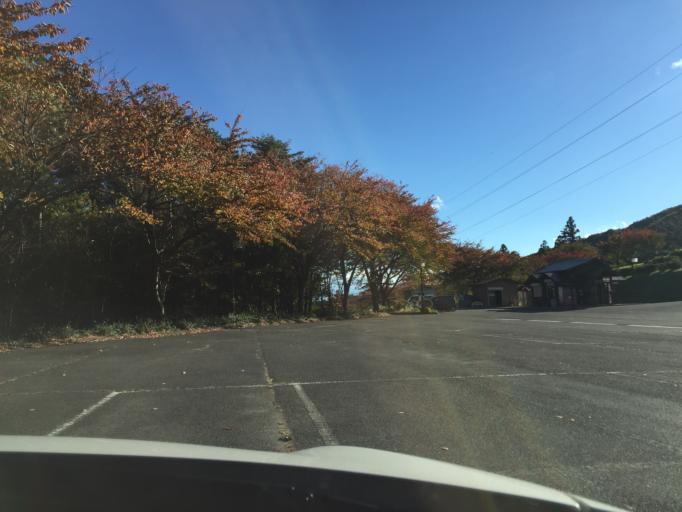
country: JP
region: Fukushima
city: Ishikawa
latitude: 37.2618
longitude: 140.5480
